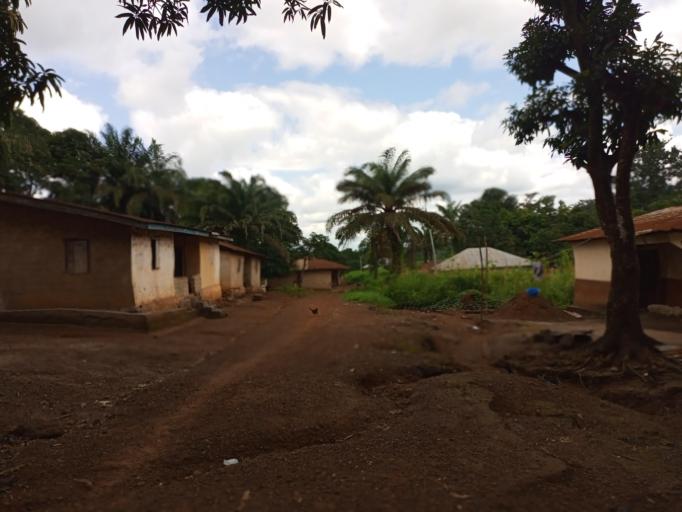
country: SL
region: Northern Province
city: Kamakwie
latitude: 9.4965
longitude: -12.2351
